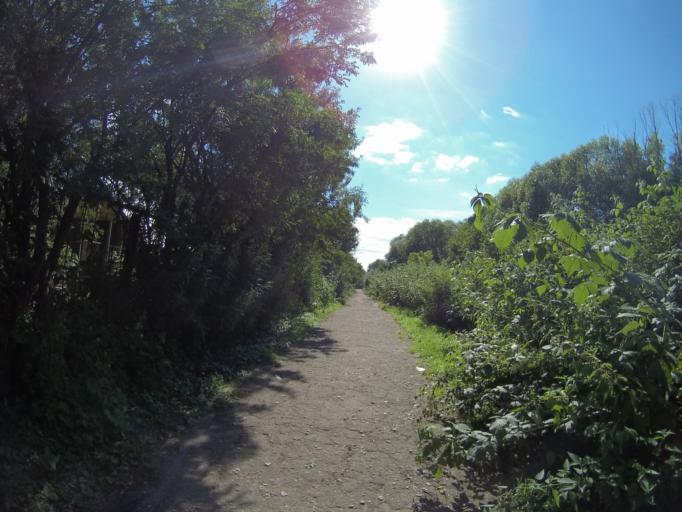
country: RU
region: Vladimir
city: Vorsha
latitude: 56.1000
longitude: 40.2077
